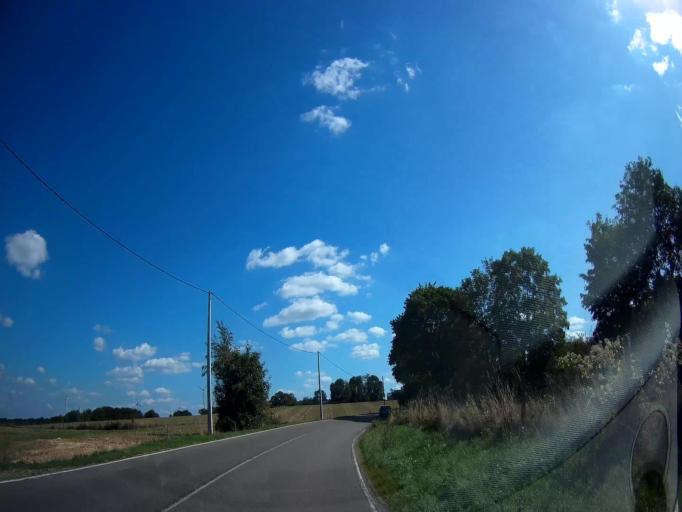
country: BE
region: Wallonia
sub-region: Province de Namur
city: Hastiere-Lavaux
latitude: 50.1879
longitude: 4.8501
